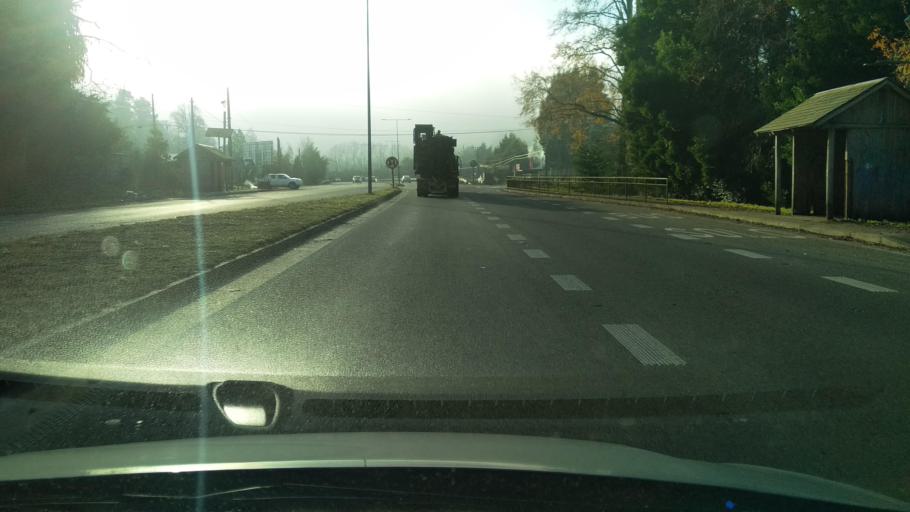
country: CL
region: Los Lagos
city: Las Animas
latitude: -39.7731
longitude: -73.2194
